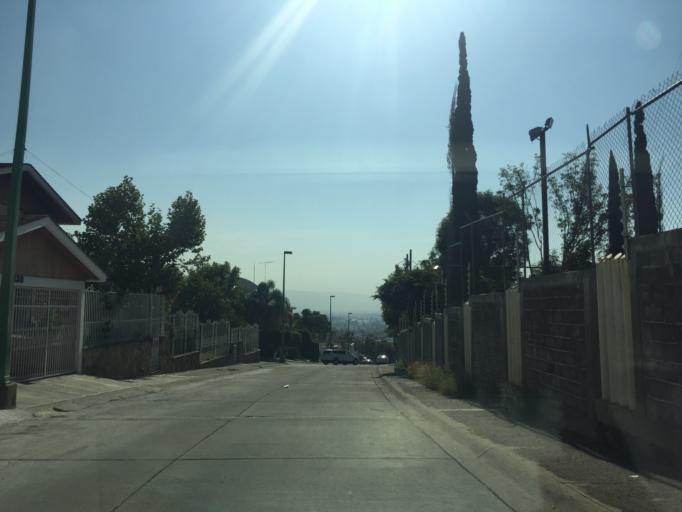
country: MX
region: Guanajuato
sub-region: Leon
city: La Ermita
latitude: 21.1541
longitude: -101.7061
